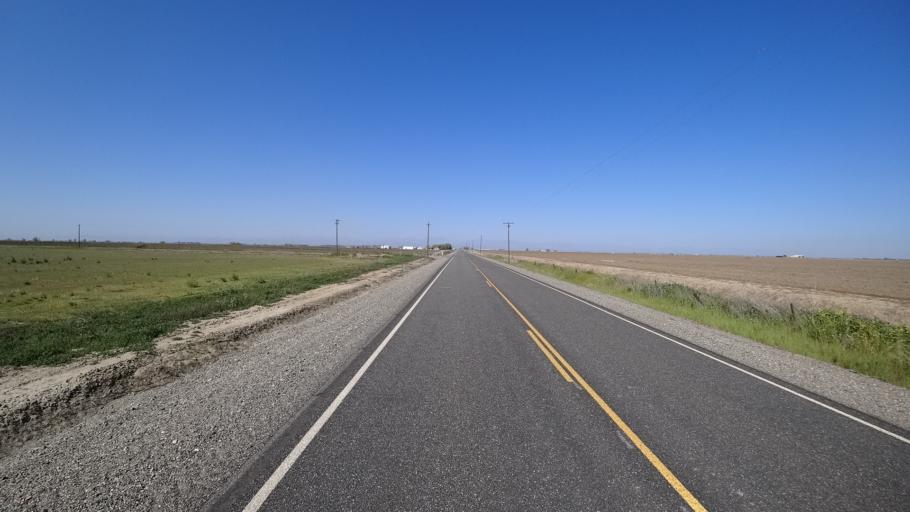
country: US
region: California
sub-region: Glenn County
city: Willows
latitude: 39.4578
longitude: -122.0628
